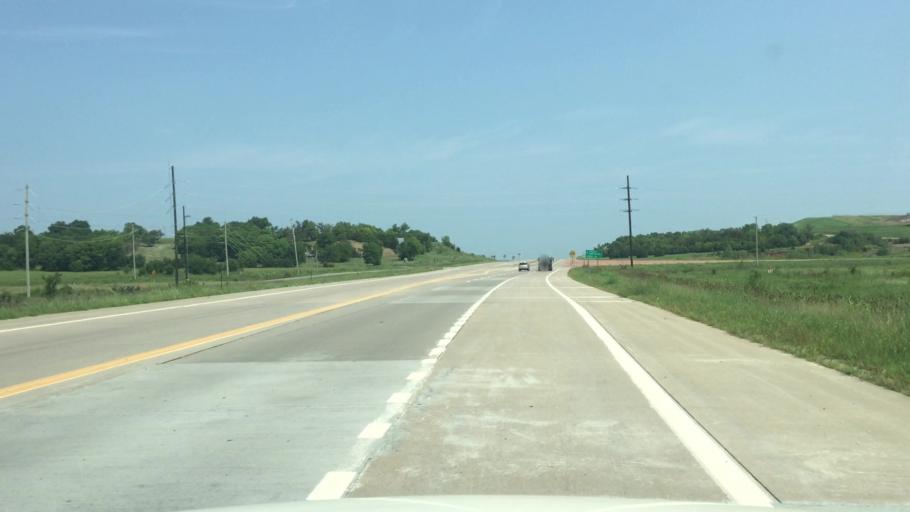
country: US
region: Kansas
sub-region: Montgomery County
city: Cherryvale
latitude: 37.2068
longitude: -95.5848
